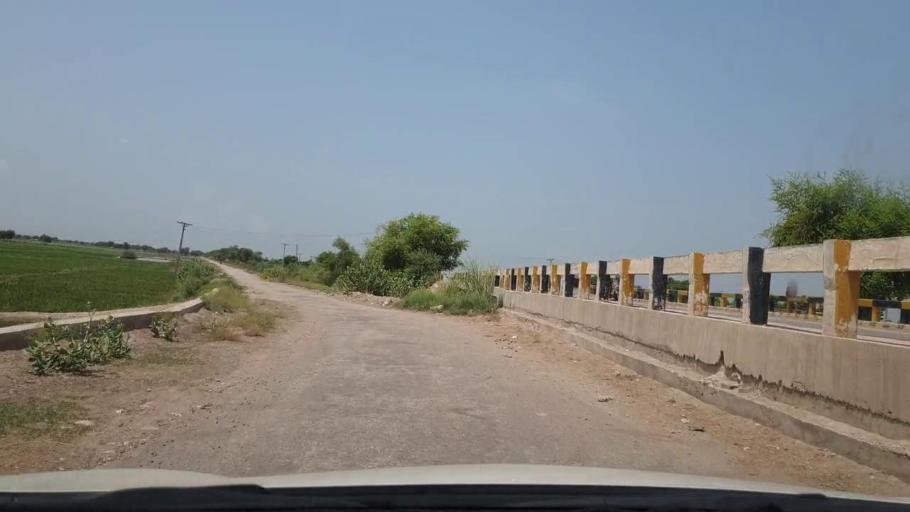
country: PK
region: Sindh
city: Ratodero
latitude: 27.8112
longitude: 68.2514
